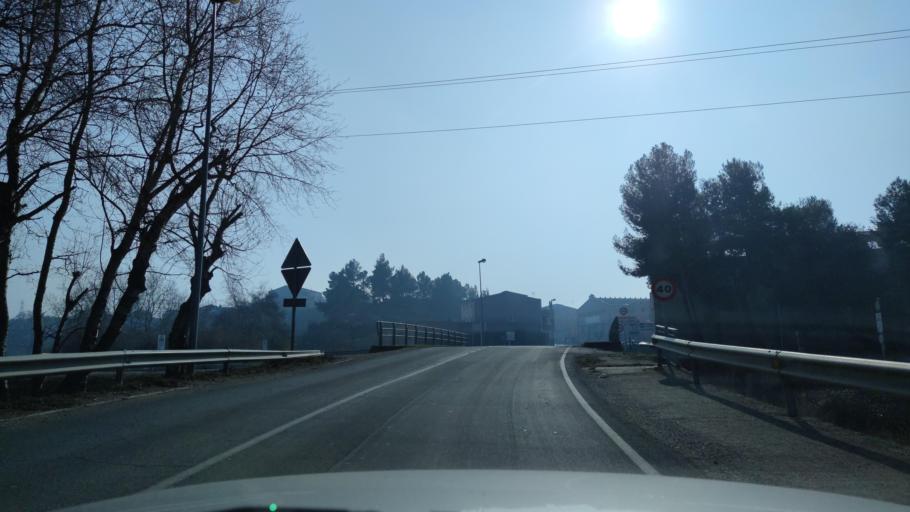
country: ES
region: Catalonia
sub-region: Provincia de Lleida
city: Sunyer
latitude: 41.5631
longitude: 0.5873
